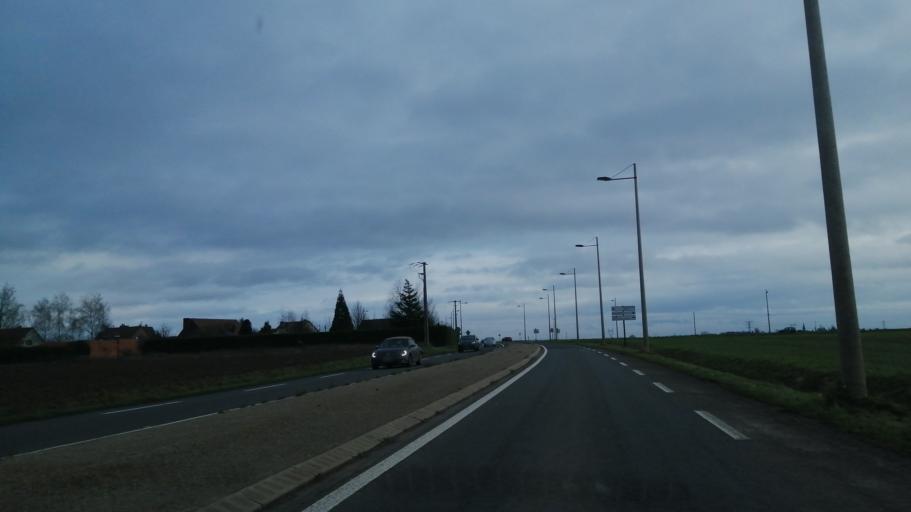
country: FR
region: Nord-Pas-de-Calais
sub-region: Departement du Pas-de-Calais
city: Mericourt
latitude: 50.3952
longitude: 2.8622
